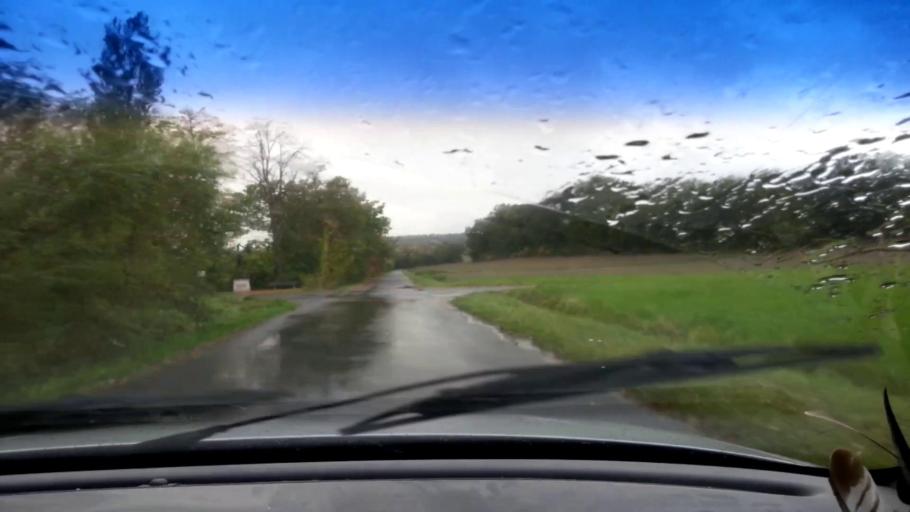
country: DE
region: Bavaria
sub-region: Upper Franconia
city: Burgebrach
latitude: 49.8301
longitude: 10.7317
